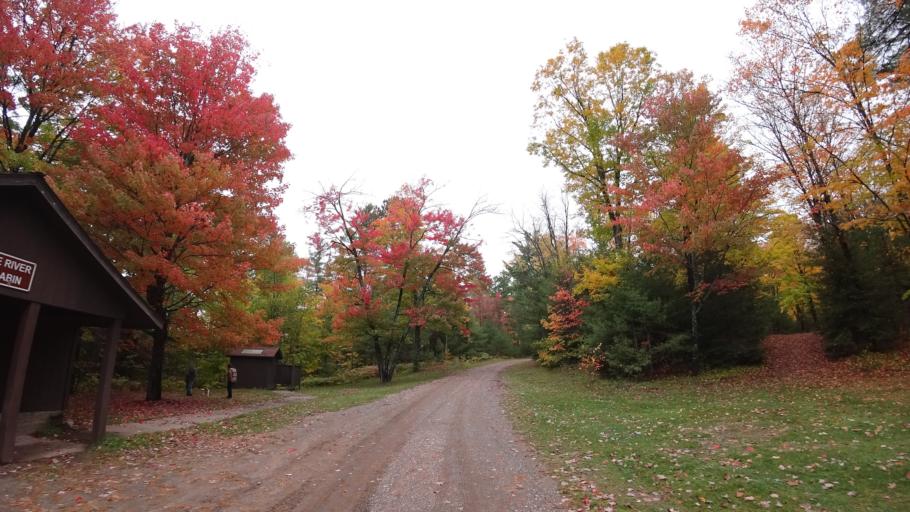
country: US
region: Michigan
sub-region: Marquette County
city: West Ishpeming
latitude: 46.5293
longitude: -88.0016
